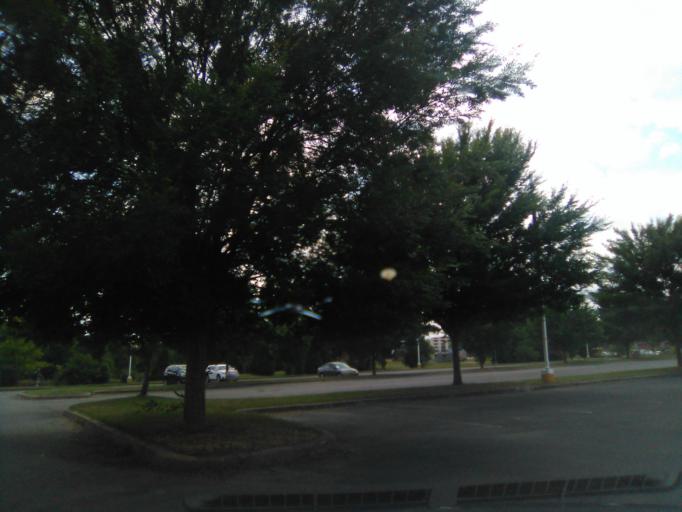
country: US
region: Tennessee
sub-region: Davidson County
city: Belle Meade
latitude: 36.1342
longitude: -86.8526
